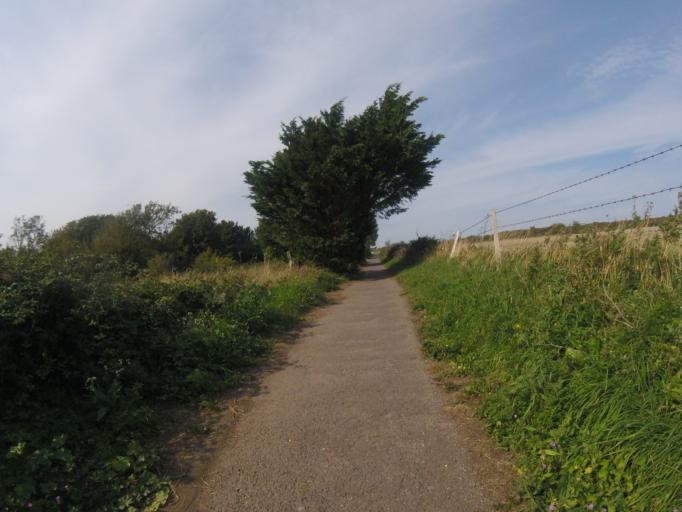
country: GB
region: England
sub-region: West Sussex
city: Fulking
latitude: 50.8721
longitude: -0.1997
